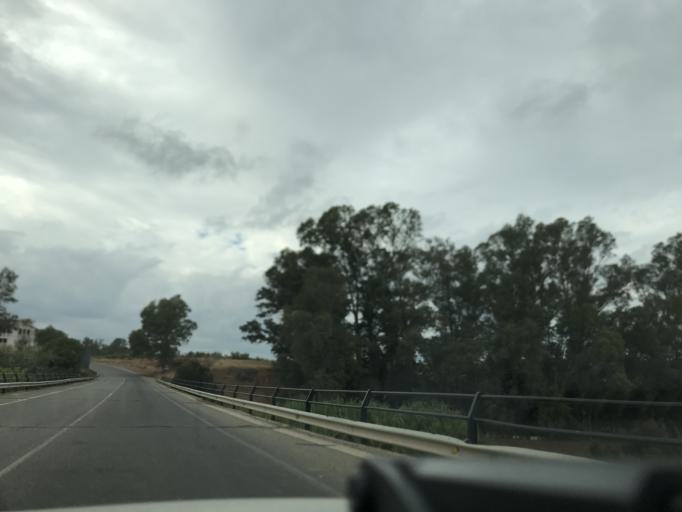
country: ES
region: Andalusia
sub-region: Provincia de Sevilla
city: Villanueva del Rio y Minas
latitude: 37.6429
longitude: -5.7388
